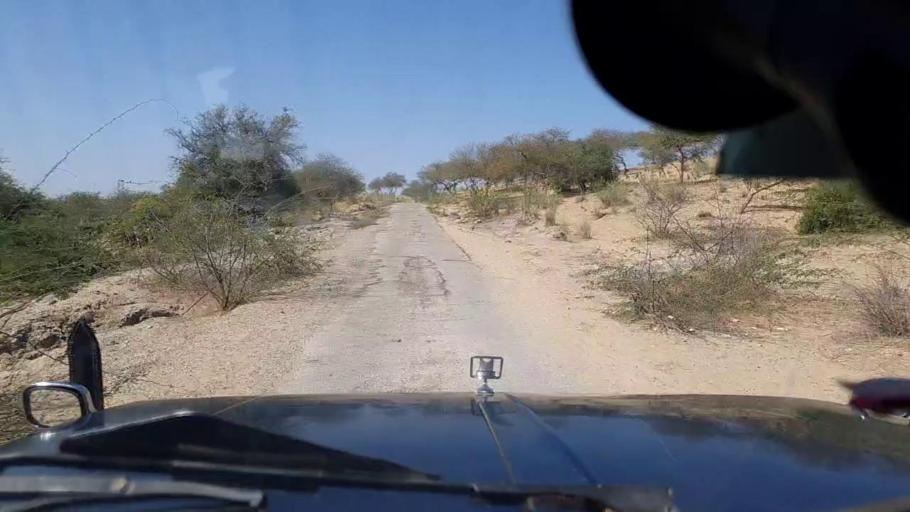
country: PK
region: Sindh
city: Mithi
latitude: 24.6117
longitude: 69.7023
